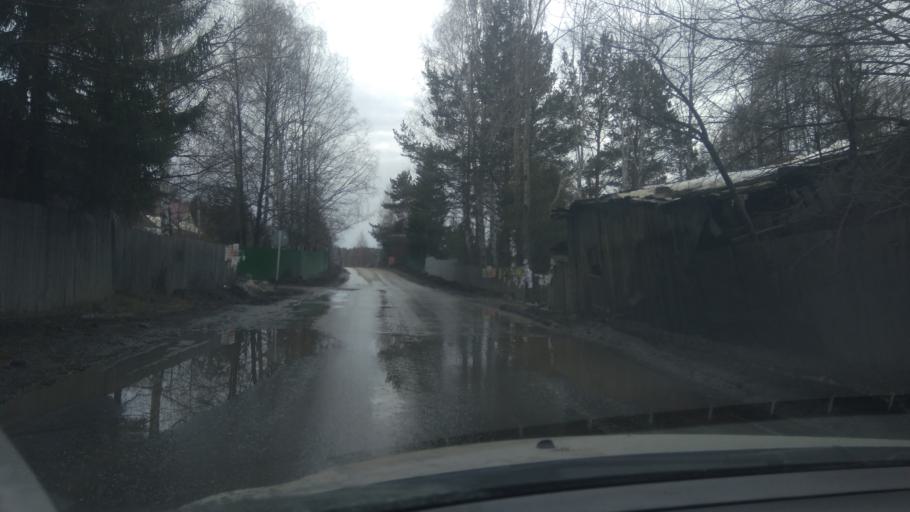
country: RU
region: Sverdlovsk
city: Severka
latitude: 56.8479
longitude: 60.3834
